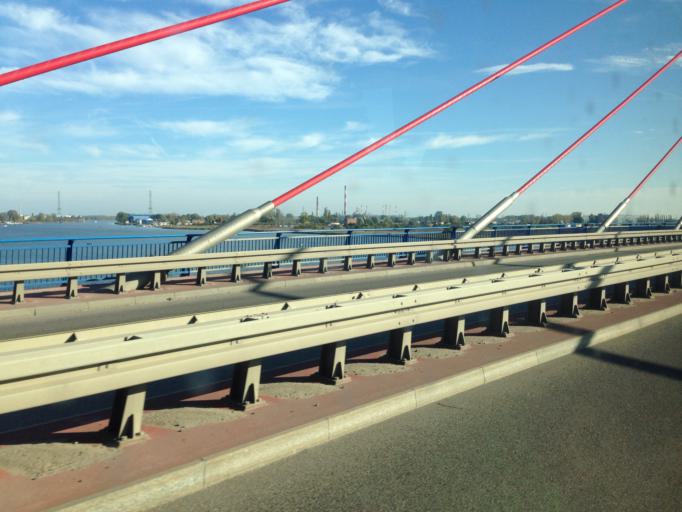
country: PL
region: Pomeranian Voivodeship
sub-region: Gdansk
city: Gdansk
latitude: 54.3570
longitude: 18.6936
